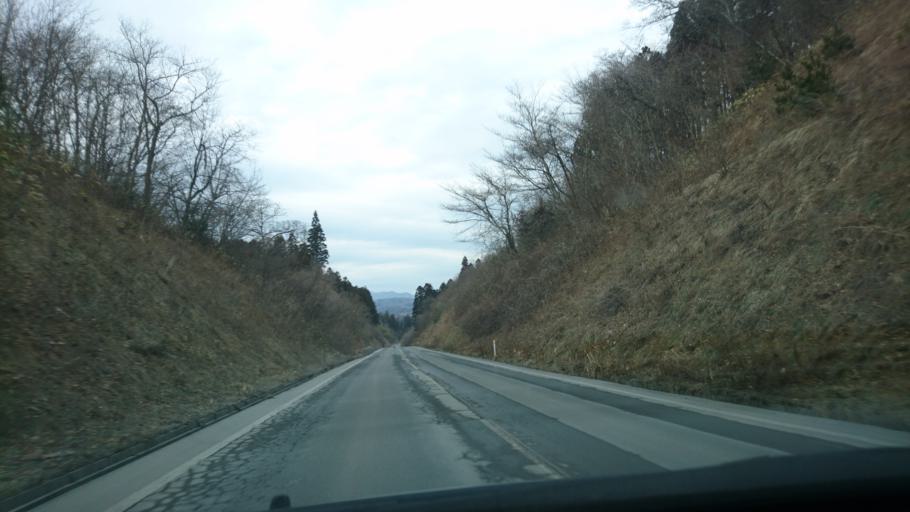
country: JP
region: Iwate
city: Ichinoseki
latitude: 38.9773
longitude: 141.3552
